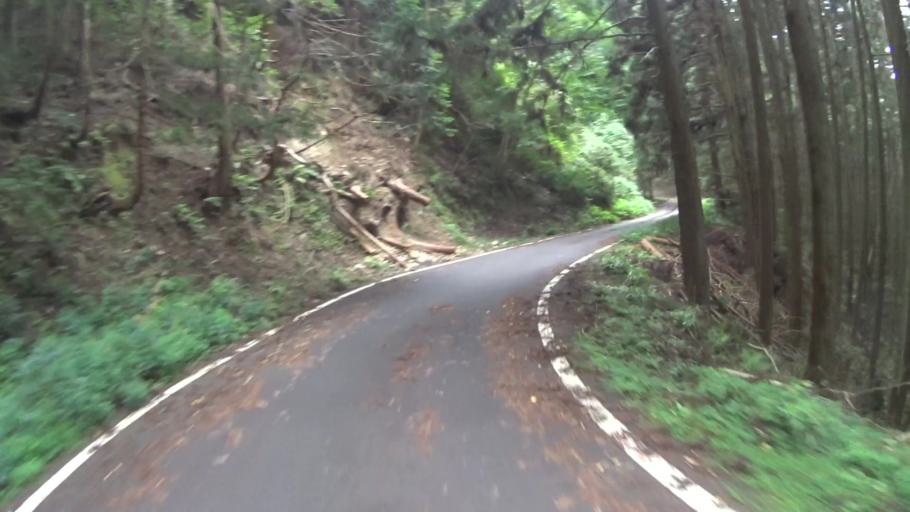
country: JP
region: Kyoto
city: Uji
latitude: 34.8504
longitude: 135.9459
